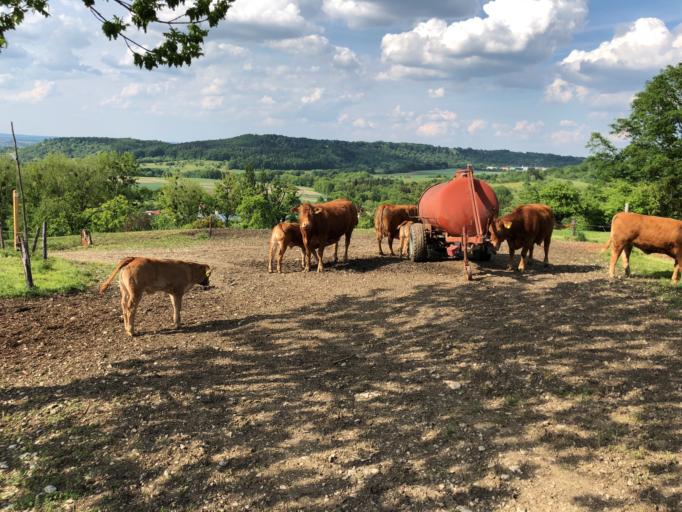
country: DE
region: Baden-Wuerttemberg
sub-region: Tuebingen Region
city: Mossingen
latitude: 48.3957
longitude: 9.0877
